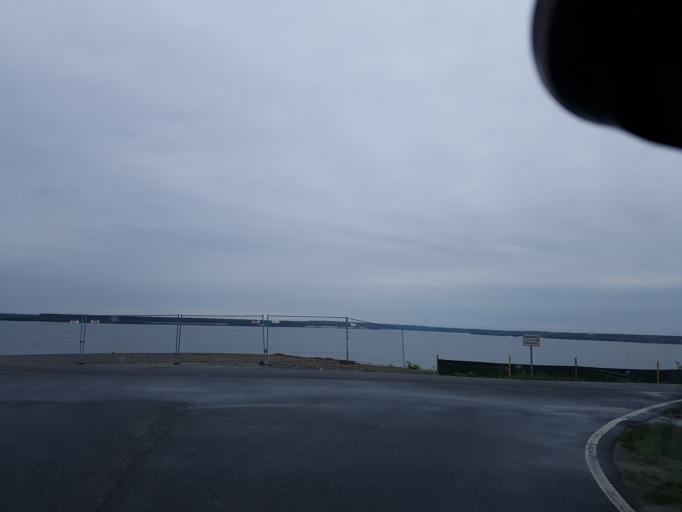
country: DE
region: Brandenburg
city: Welzow
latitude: 51.5628
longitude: 14.1104
